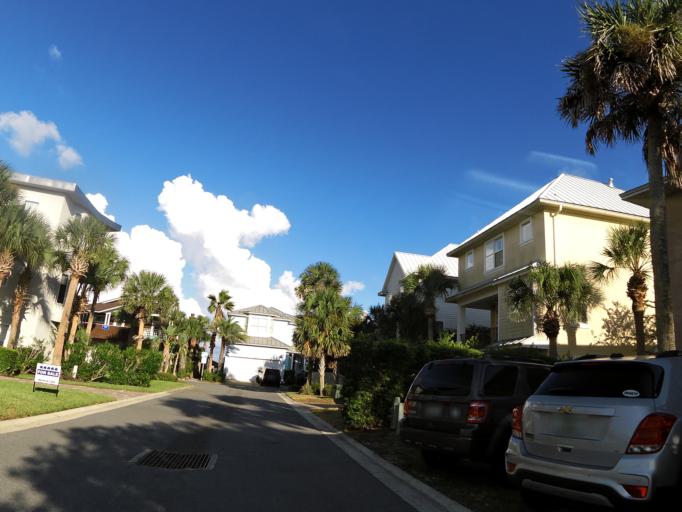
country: US
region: Florida
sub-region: Saint Johns County
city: Ponte Vedra Beach
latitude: 30.2662
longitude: -81.3848
